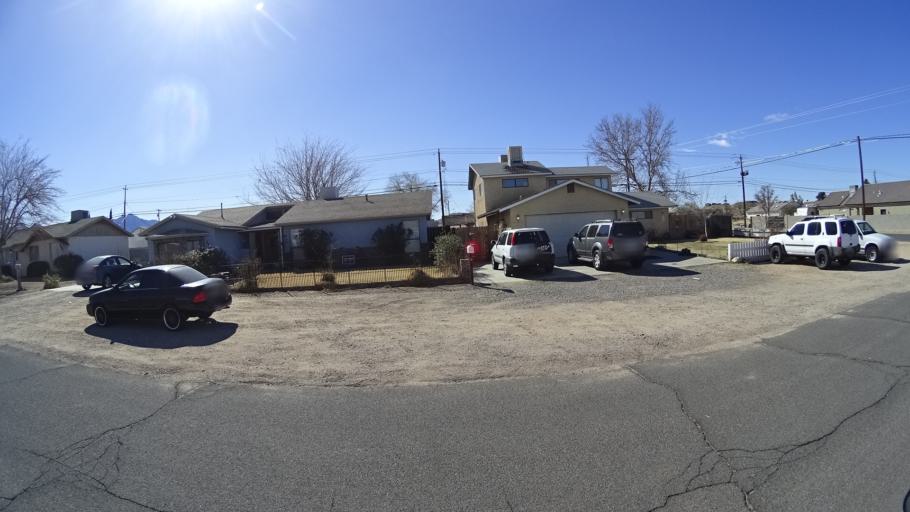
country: US
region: Arizona
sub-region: Mohave County
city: Kingman
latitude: 35.1931
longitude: -114.0198
